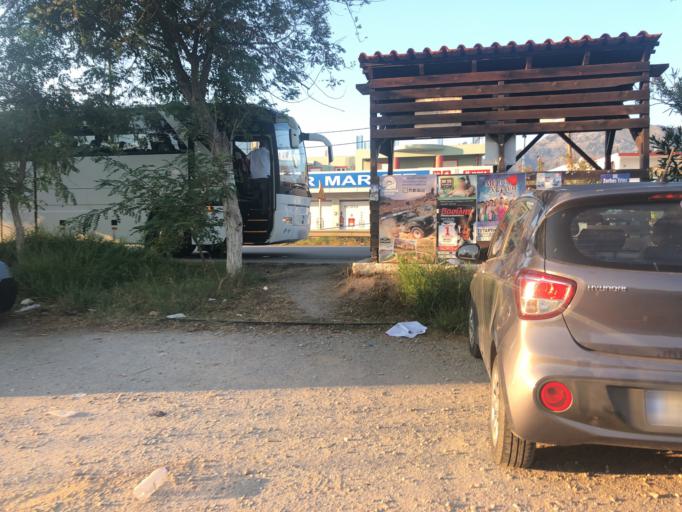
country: GR
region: Crete
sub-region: Nomos Chanias
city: Georgioupolis
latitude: 35.3513
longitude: 24.3006
